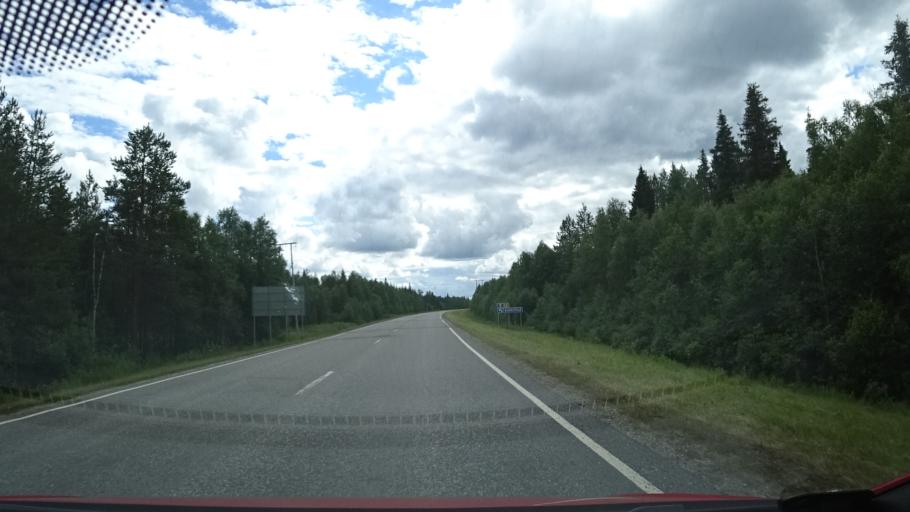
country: FI
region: Lapland
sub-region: Tunturi-Lappi
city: Kittilae
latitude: 67.6310
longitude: 24.9309
